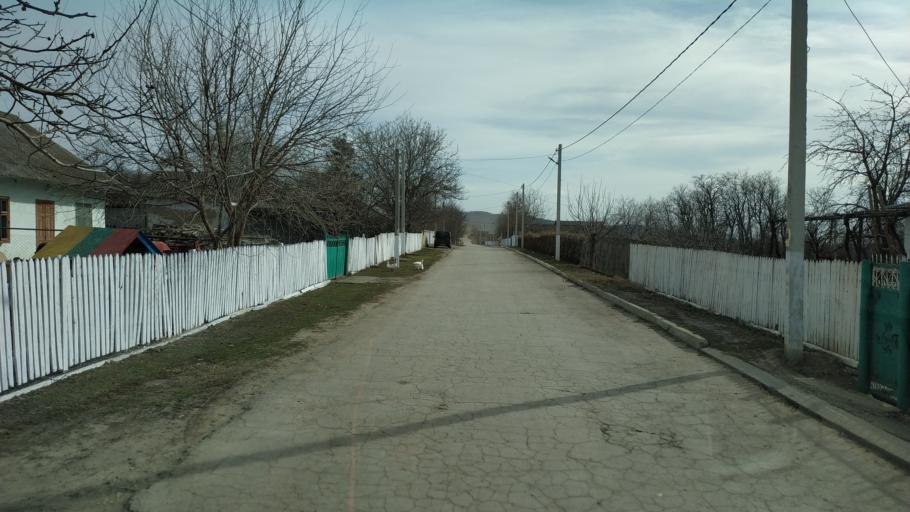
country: RO
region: Vaslui
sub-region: Comuna Dranceni
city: Dranceni
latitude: 46.8722
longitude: 28.2068
